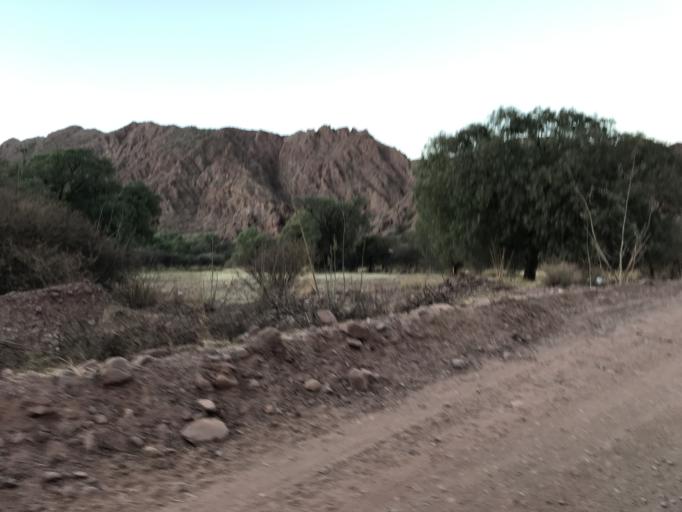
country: BO
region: Potosi
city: Tupiza
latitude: -21.3976
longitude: -65.7420
